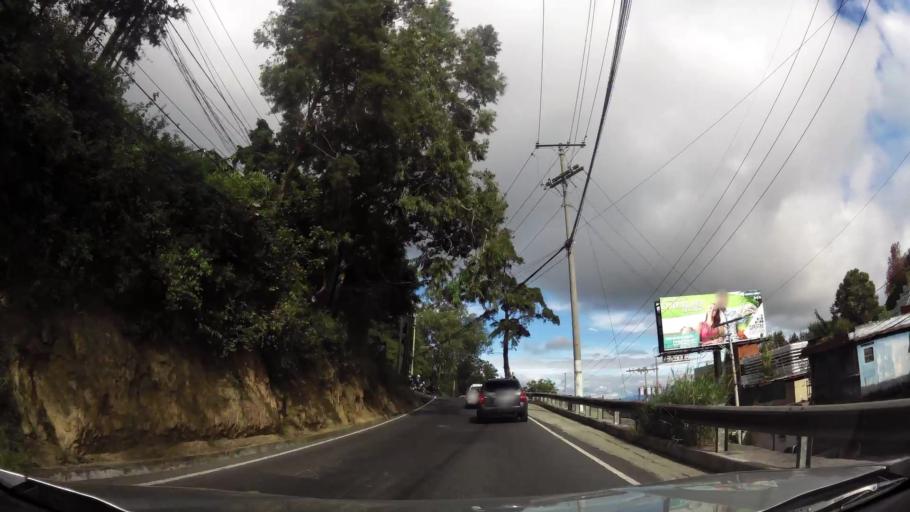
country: GT
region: Guatemala
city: Santa Catarina Pinula
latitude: 14.5724
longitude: -90.4884
